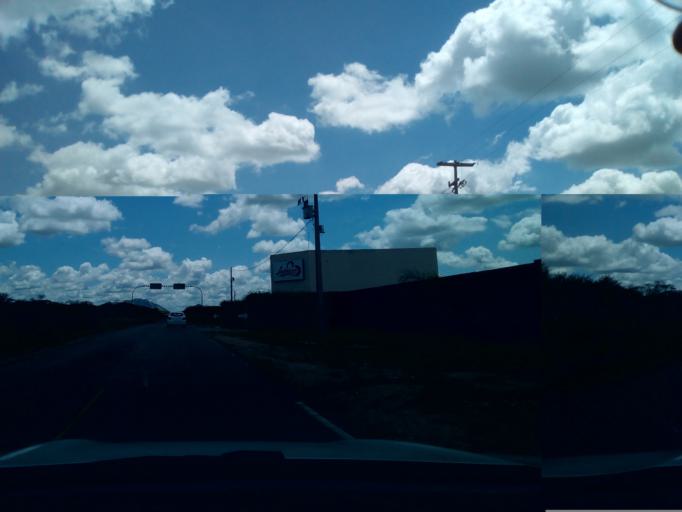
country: BR
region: Rio Grande do Norte
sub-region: Jardim De Piranhas
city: Jardim de Piranhas
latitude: -6.3725
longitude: -37.3844
